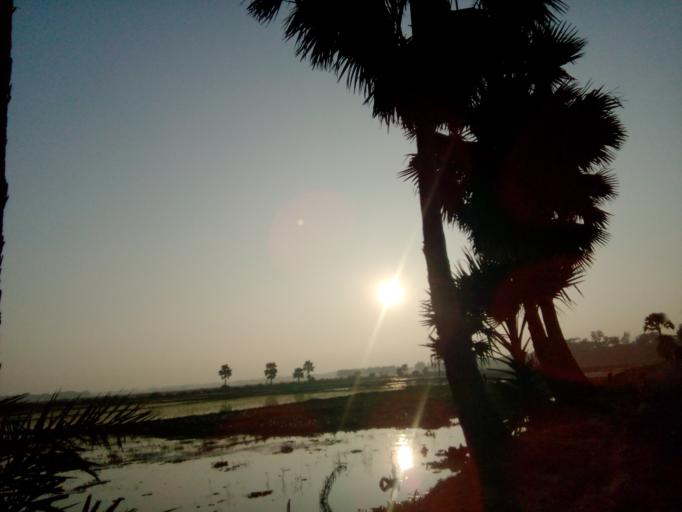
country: BD
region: Chittagong
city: Comilla
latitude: 23.4030
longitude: 91.1896
